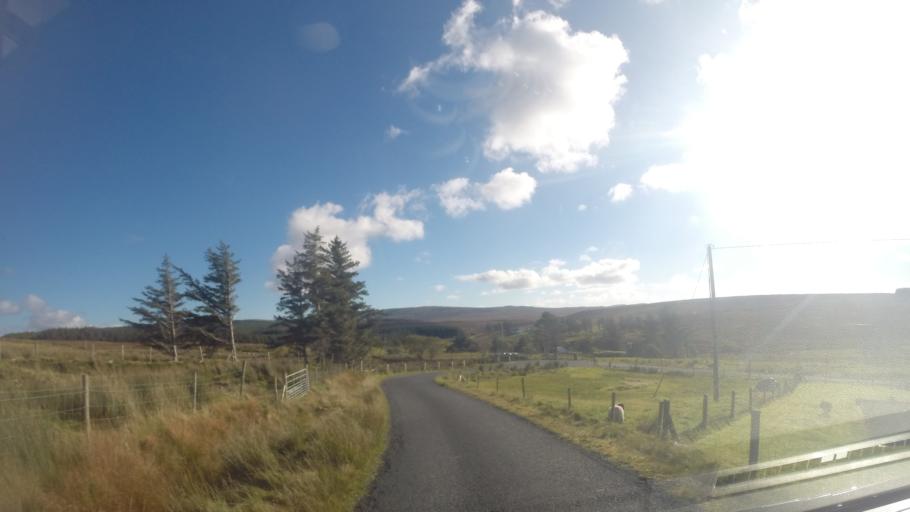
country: IE
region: Ulster
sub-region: County Donegal
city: Killybegs
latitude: 54.7188
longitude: -8.5812
